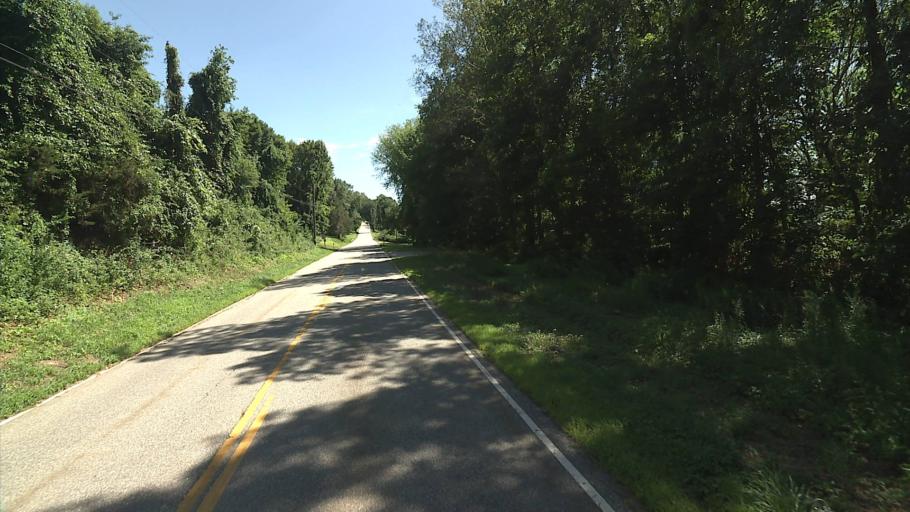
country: US
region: Connecticut
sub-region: New London County
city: Baltic
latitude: 41.6467
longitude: -72.0910
